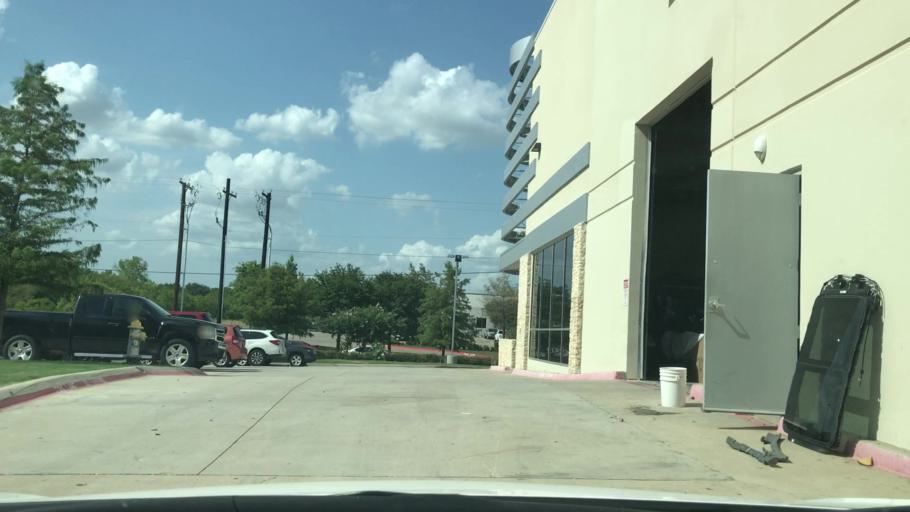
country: US
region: Texas
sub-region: Dallas County
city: Addison
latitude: 32.9713
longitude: -96.8452
